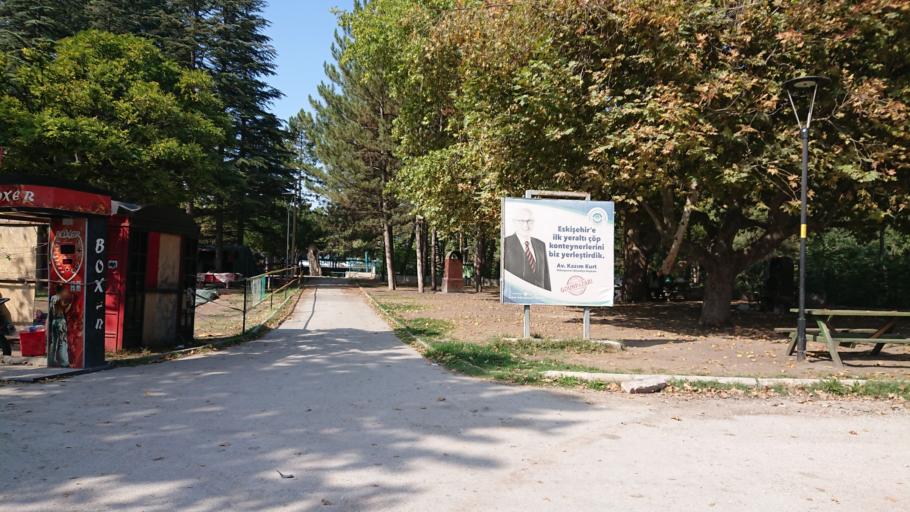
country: TR
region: Eskisehir
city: Eskisehir
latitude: 39.7437
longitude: 30.4668
